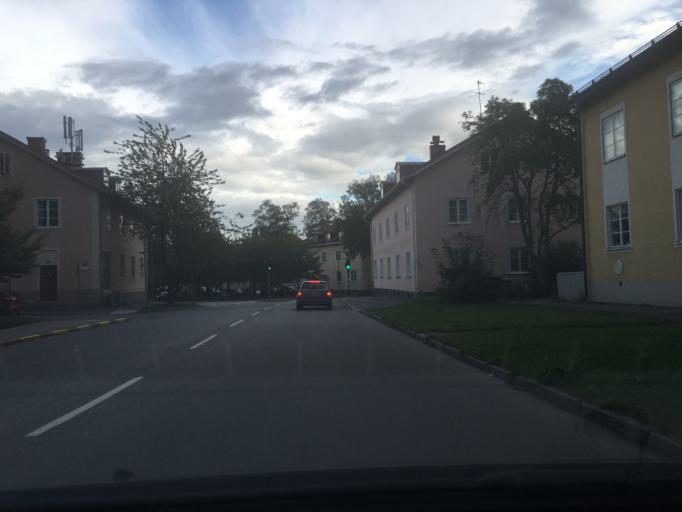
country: SE
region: Stockholm
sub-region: Stockholms Kommun
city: Bromma
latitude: 59.3288
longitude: 17.9684
